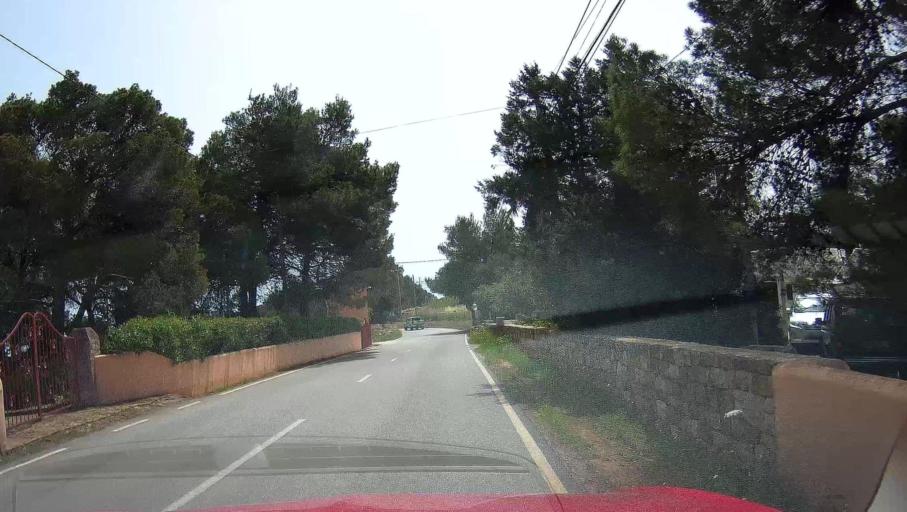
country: ES
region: Balearic Islands
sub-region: Illes Balears
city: Santa Eularia des Riu
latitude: 39.0115
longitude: 1.5658
